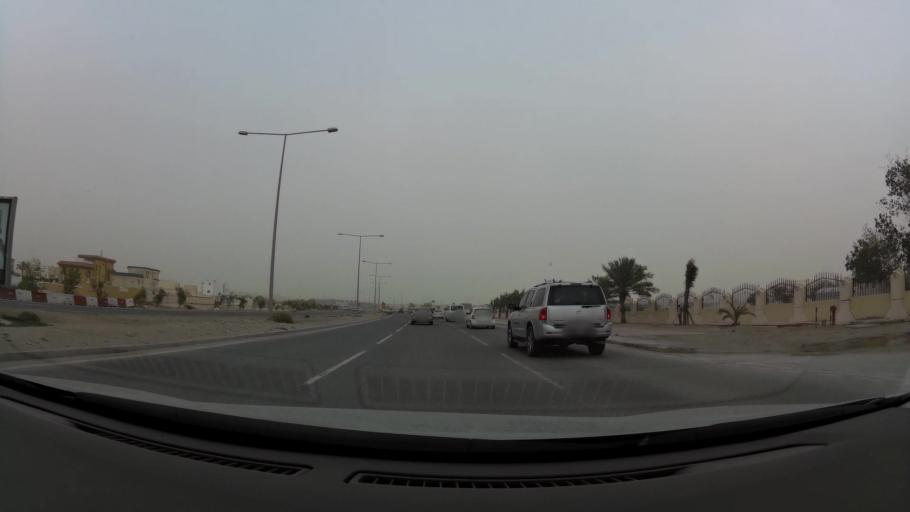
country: QA
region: Baladiyat ad Dawhah
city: Doha
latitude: 25.2269
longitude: 51.4961
